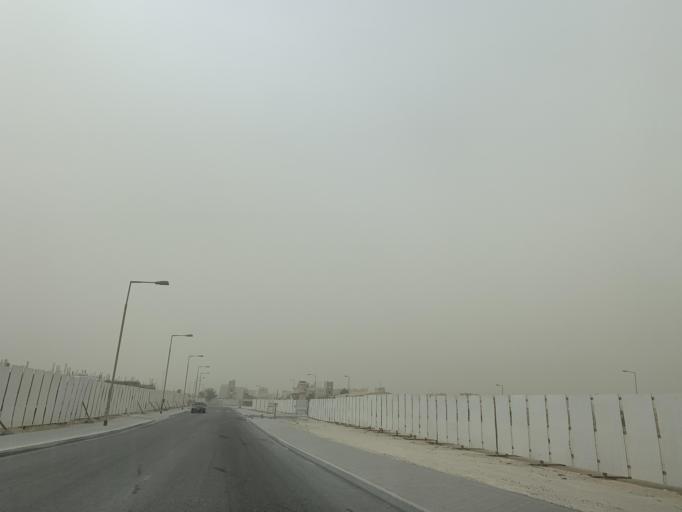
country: BH
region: Central Governorate
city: Madinat Hamad
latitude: 26.1234
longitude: 50.5107
